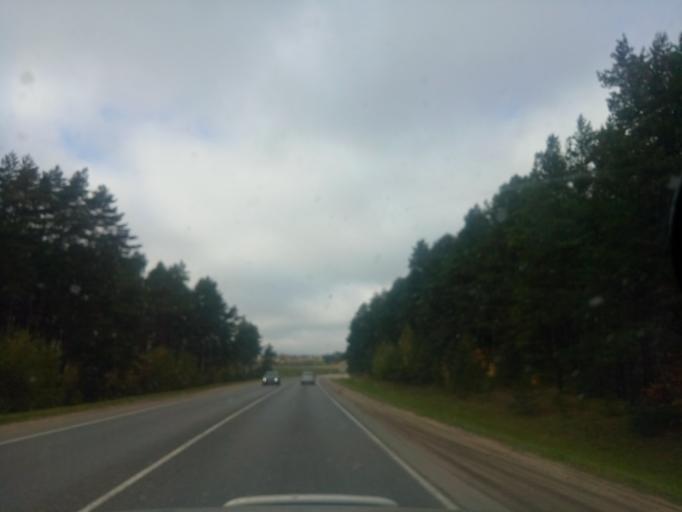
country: BY
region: Minsk
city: Zaslawye
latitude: 53.9924
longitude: 27.2996
